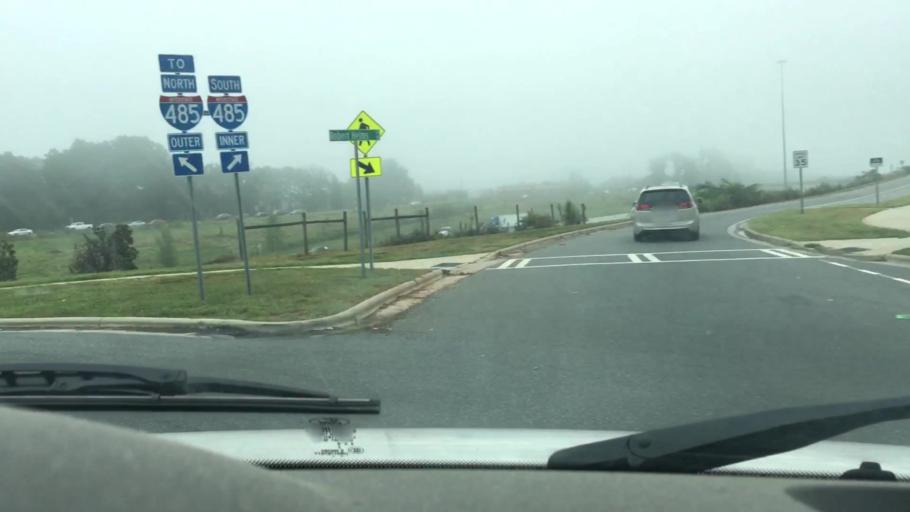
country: US
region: North Carolina
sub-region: Mecklenburg County
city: Huntersville
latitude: 35.3683
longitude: -80.7894
